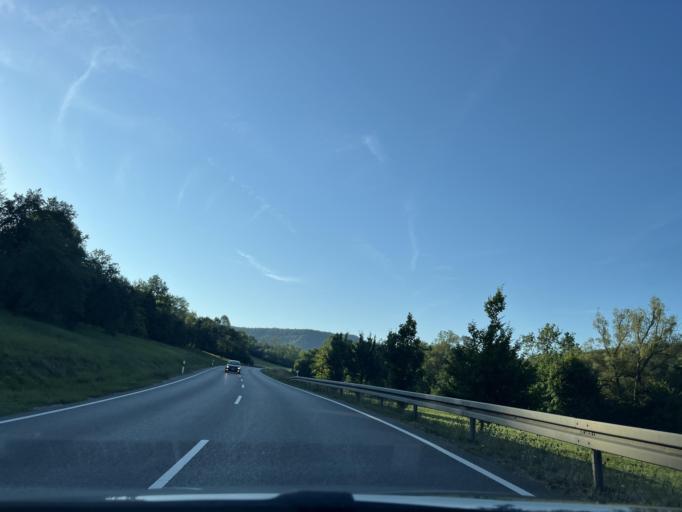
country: DE
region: Baden-Wuerttemberg
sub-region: Tuebingen Region
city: Jungingen
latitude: 48.3257
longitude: 9.0485
